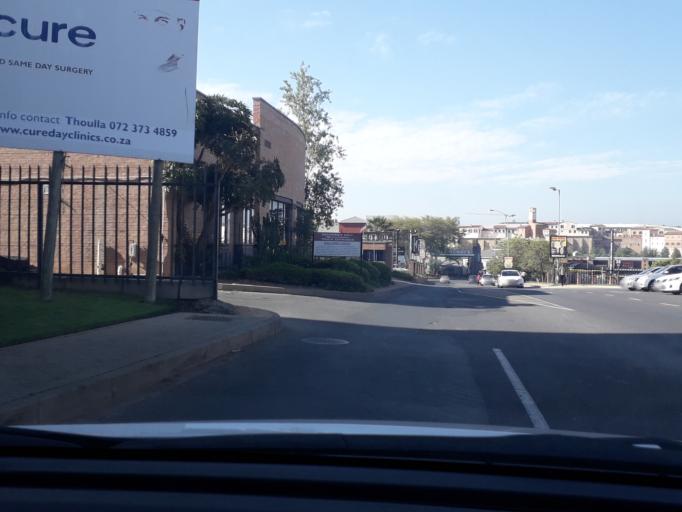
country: ZA
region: Gauteng
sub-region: City of Johannesburg Metropolitan Municipality
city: Diepsloot
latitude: -26.0190
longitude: 28.0140
